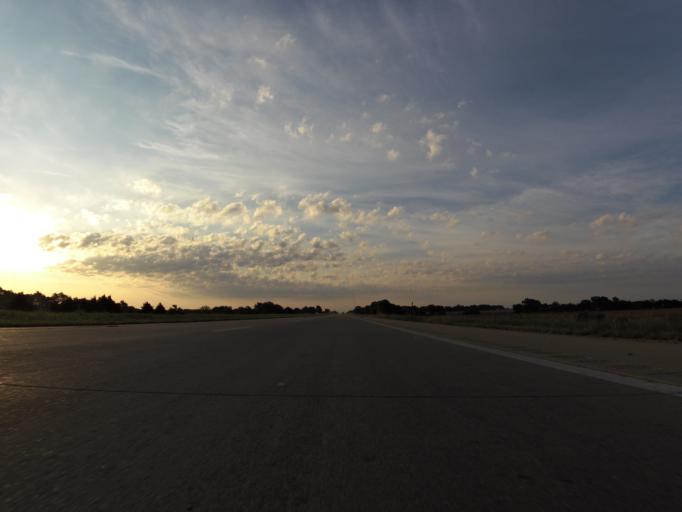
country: US
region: Kansas
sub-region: Reno County
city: Haven
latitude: 37.9233
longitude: -97.8366
